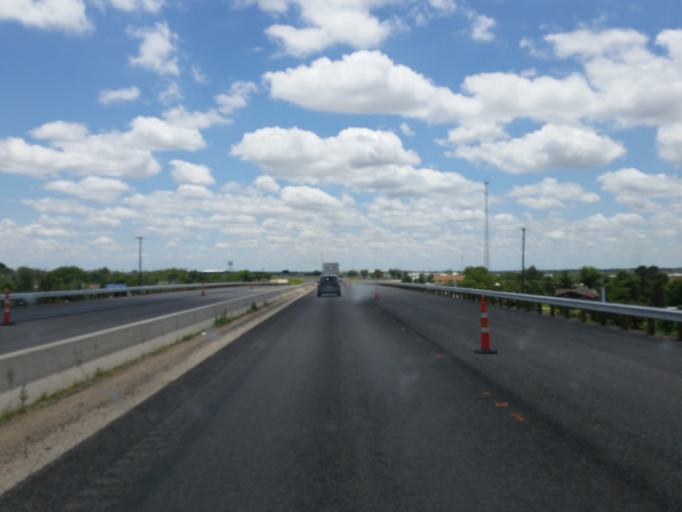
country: US
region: Texas
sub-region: Scurry County
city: Snyder
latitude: 32.7480
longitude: -100.9247
